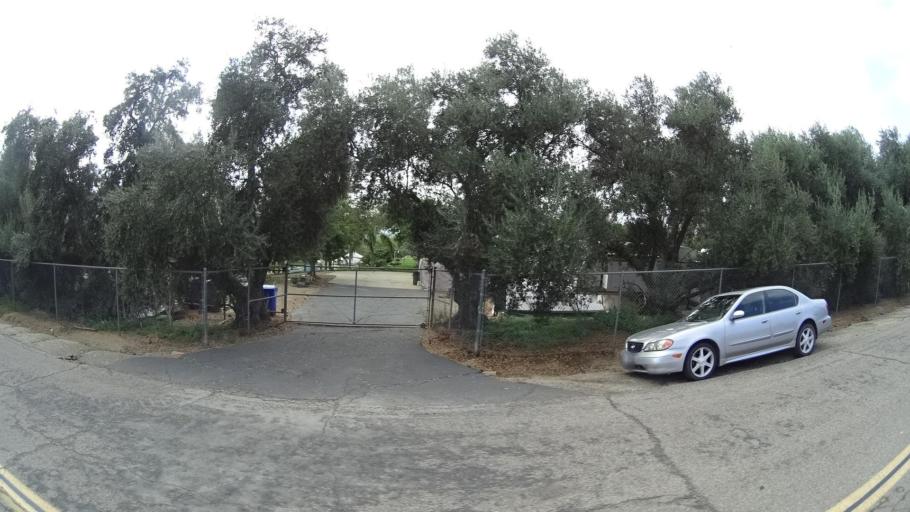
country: US
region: California
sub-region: San Diego County
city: Ramona
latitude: 33.0325
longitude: -116.8374
